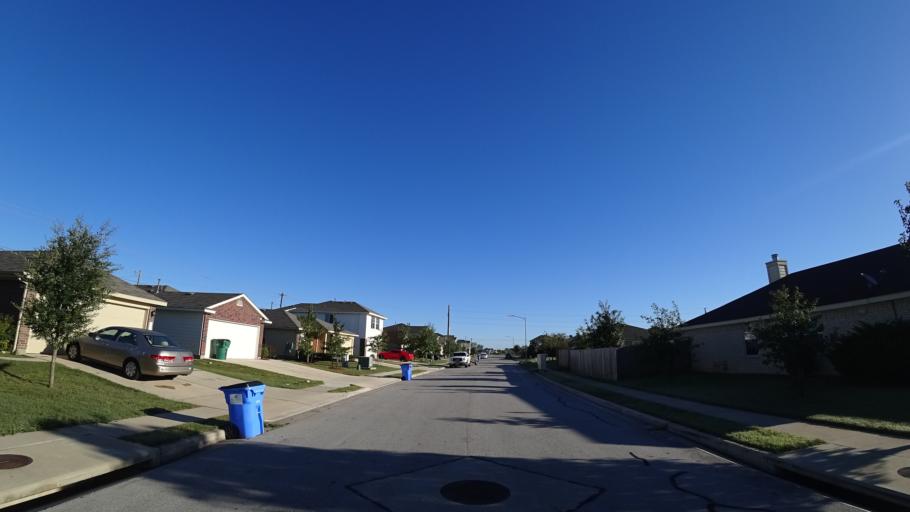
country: US
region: Texas
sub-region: Travis County
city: Hornsby Bend
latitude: 30.2148
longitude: -97.6379
